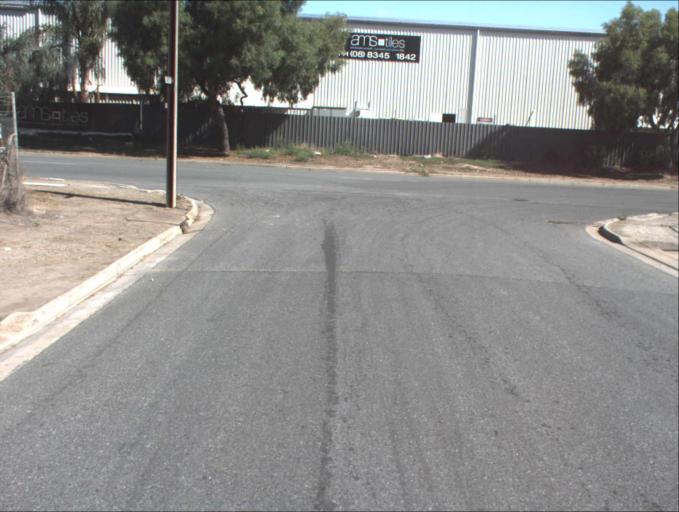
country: AU
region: South Australia
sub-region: Charles Sturt
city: Woodville North
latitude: -34.8386
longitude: 138.5608
